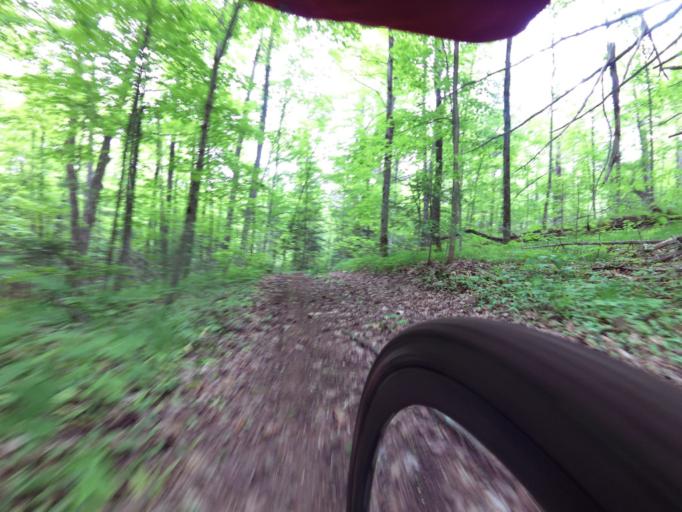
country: CA
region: Ontario
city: Arnprior
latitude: 45.1871
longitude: -76.5316
